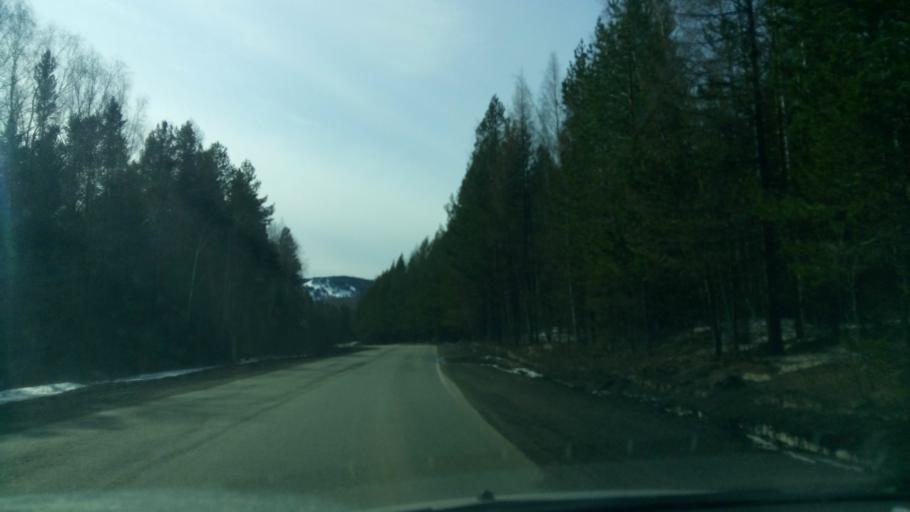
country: RU
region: Sverdlovsk
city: Chernoistochinsk
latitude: 57.7048
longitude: 59.7747
